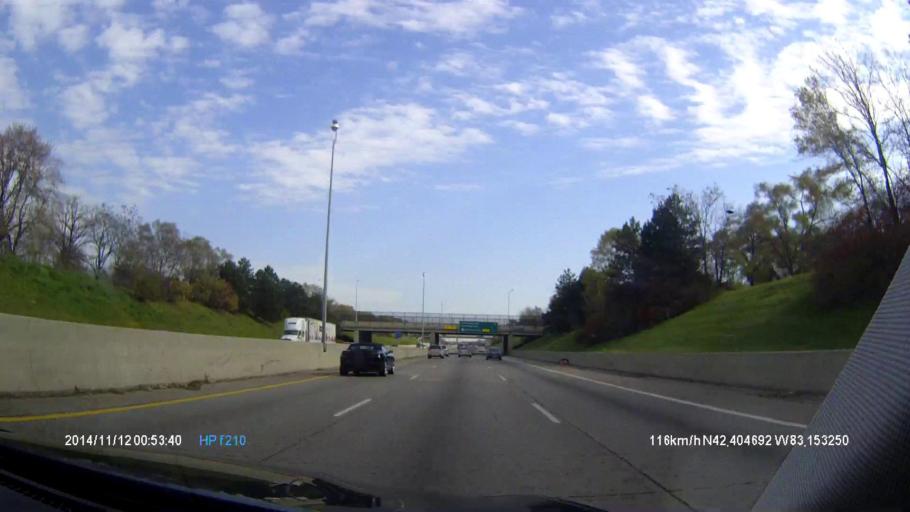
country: US
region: Michigan
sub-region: Wayne County
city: Highland Park
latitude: 42.4047
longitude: -83.1530
